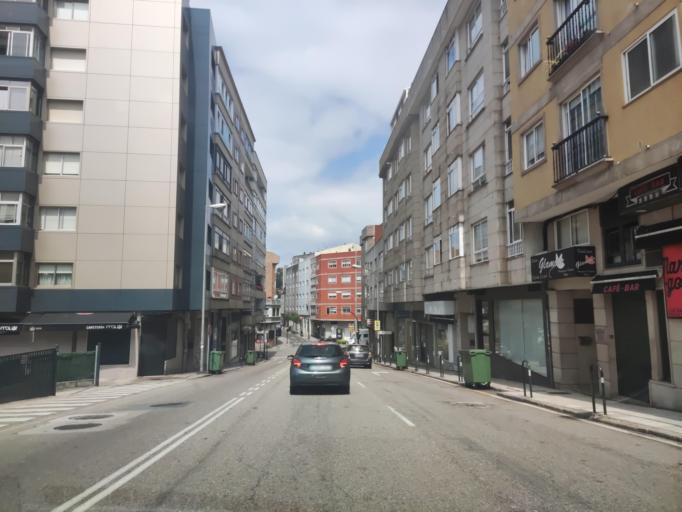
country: ES
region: Galicia
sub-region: Provincia de Pontevedra
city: Vigo
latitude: 42.2492
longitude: -8.6952
